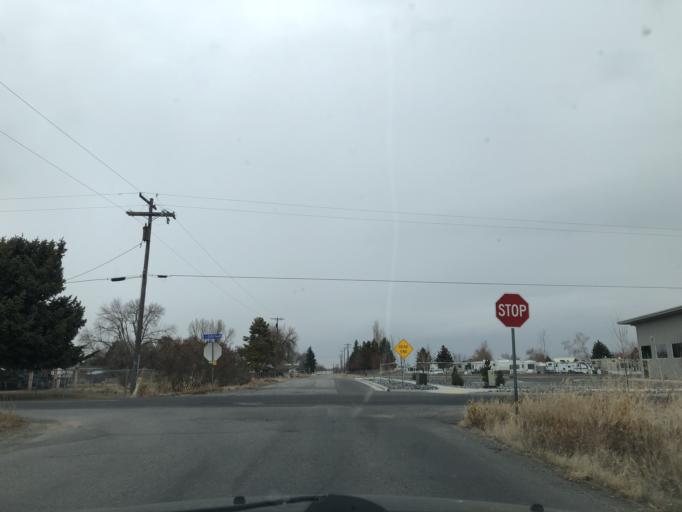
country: US
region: Utah
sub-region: Cache County
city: Nibley
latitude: 41.6926
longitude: -111.8622
